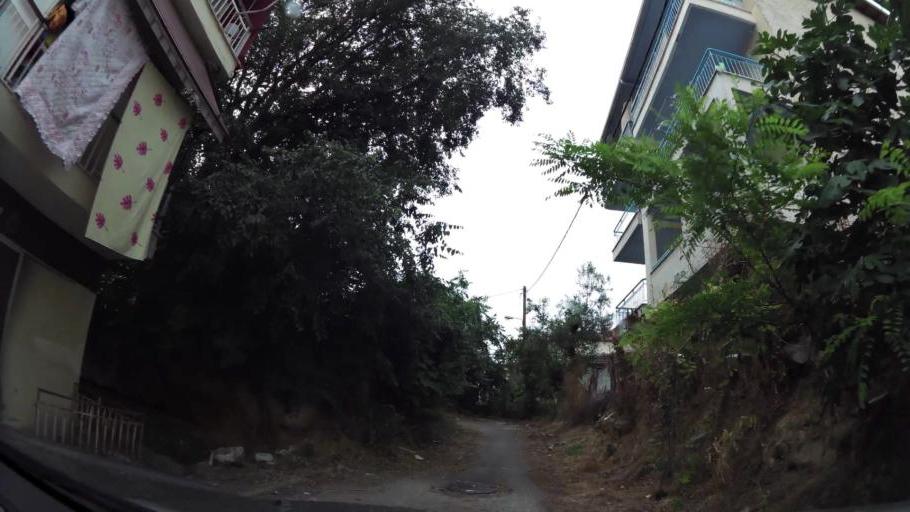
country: GR
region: Central Macedonia
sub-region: Nomos Imathias
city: Veroia
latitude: 40.5267
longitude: 22.1970
